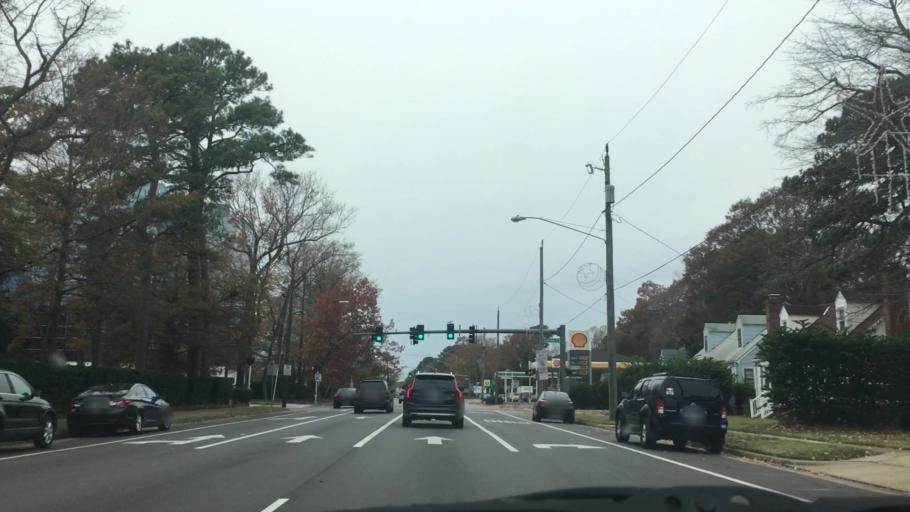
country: US
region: Virginia
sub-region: City of Virginia Beach
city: Virginia Beach
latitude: 36.8488
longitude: -75.9836
